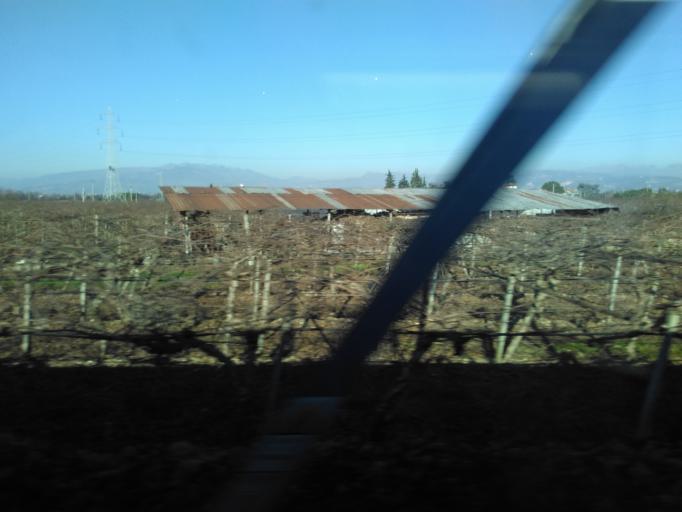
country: IT
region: Veneto
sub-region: Provincia di Verona
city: Caselle
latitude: 45.4272
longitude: 10.9240
